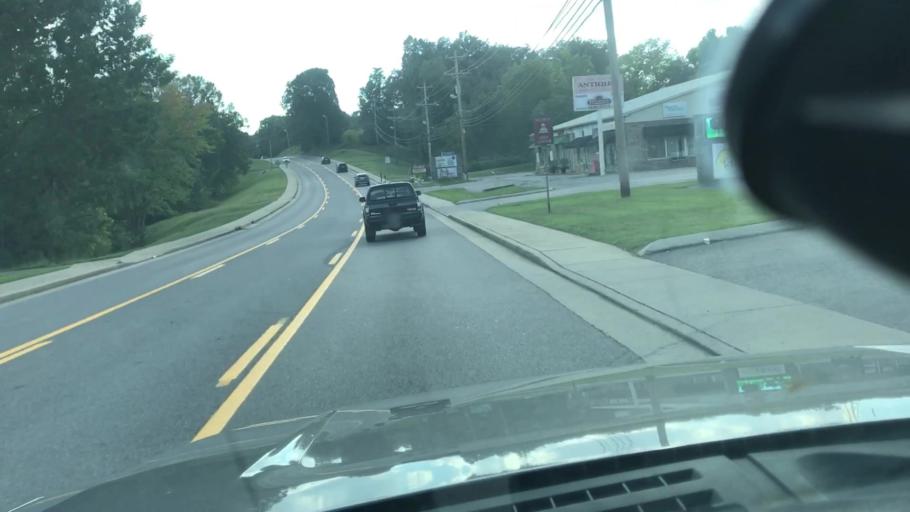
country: US
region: Tennessee
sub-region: Williamson County
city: Fairview
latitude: 35.9812
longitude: -87.1224
